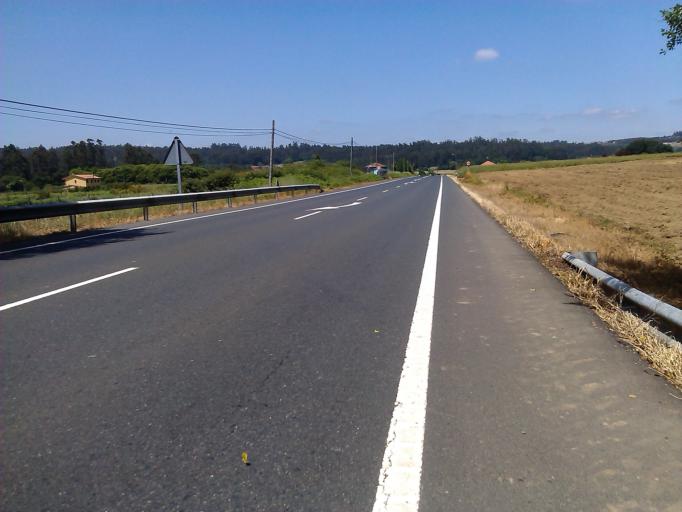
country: ES
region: Galicia
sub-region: Provincia da Coruna
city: Touro
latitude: 42.9007
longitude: -8.3842
